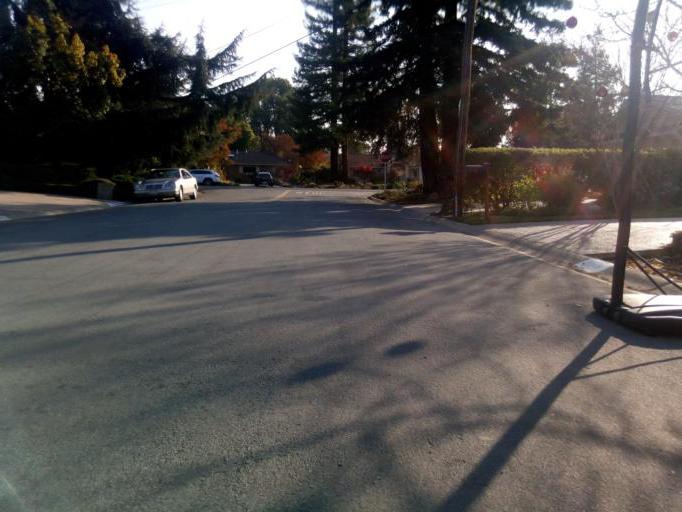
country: US
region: California
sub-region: Santa Clara County
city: Mountain View
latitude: 37.3721
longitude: -122.0690
